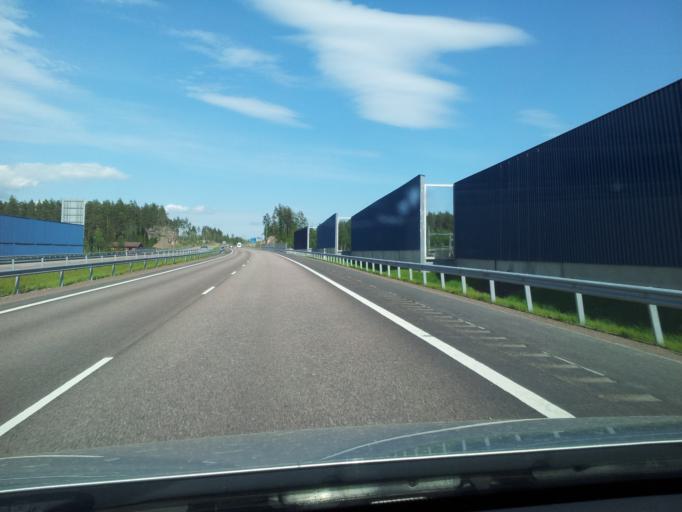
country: FI
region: Uusimaa
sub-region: Loviisa
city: Lovisa
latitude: 60.4680
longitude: 26.2283
